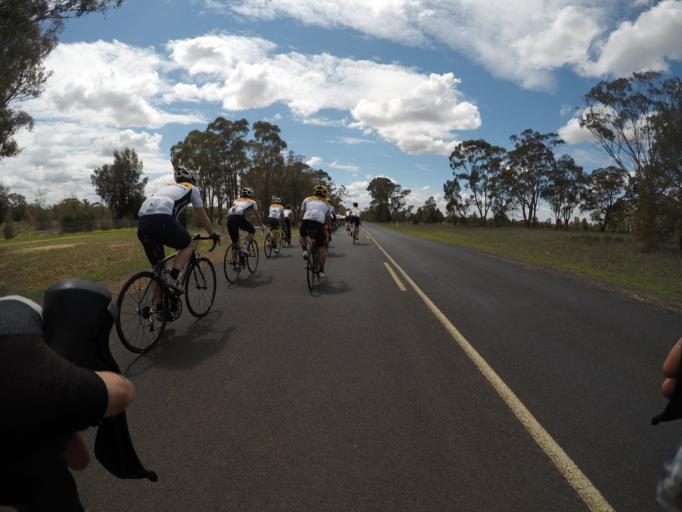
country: AU
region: New South Wales
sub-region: Dubbo Municipality
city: Dubbo
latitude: -32.3053
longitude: 148.5943
